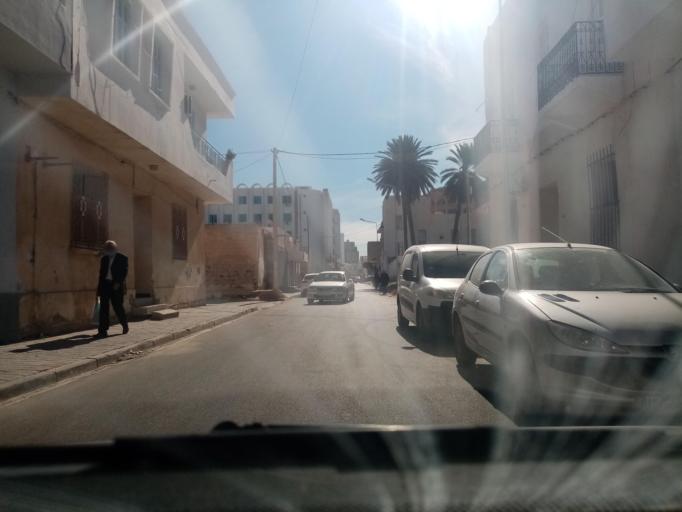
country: TN
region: Qabis
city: Gabes
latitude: 33.8885
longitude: 10.1037
